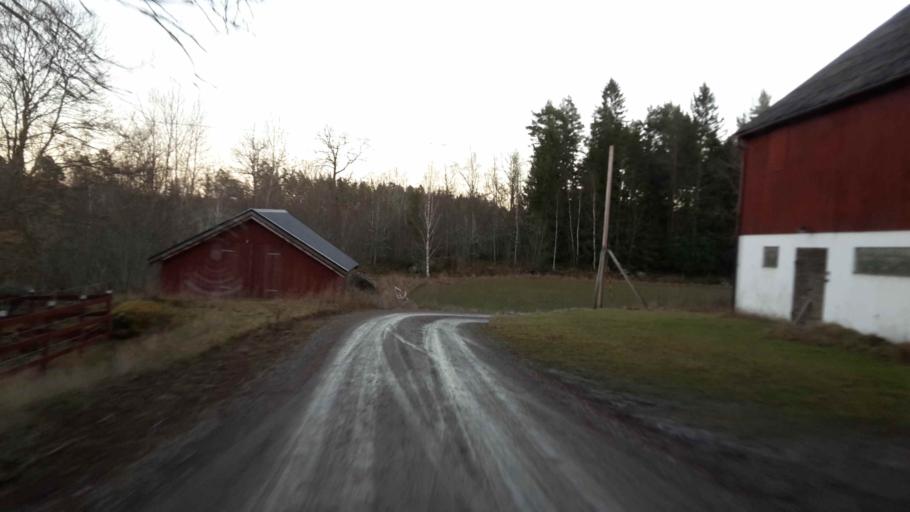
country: SE
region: OEstergoetland
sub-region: Atvidabergs Kommun
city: Atvidaberg
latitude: 58.2679
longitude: 16.0723
